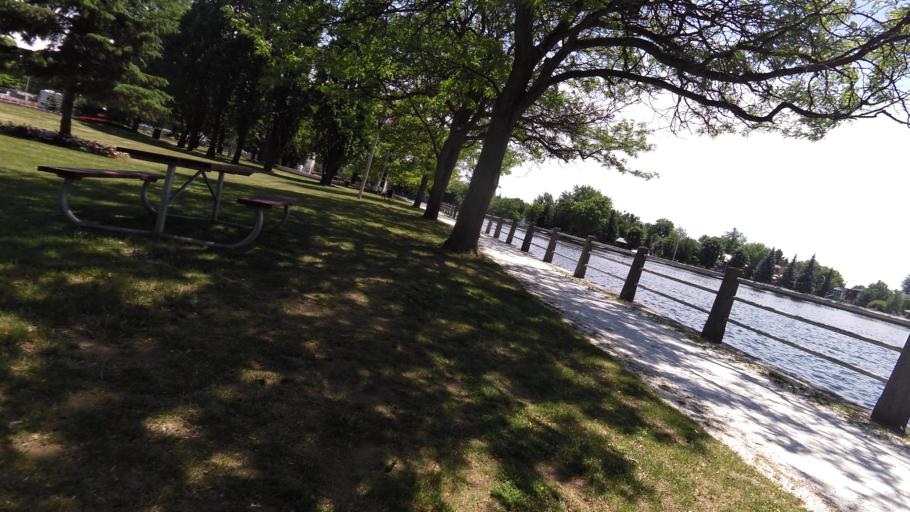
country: CA
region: Ontario
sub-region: Lanark County
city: Smiths Falls
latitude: 44.8973
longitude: -76.0235
